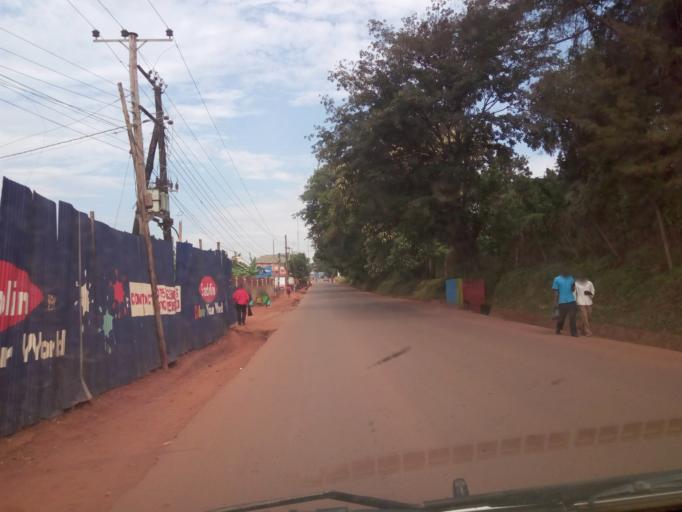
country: UG
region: Central Region
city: Kampala Central Division
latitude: 0.3456
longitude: 32.5798
